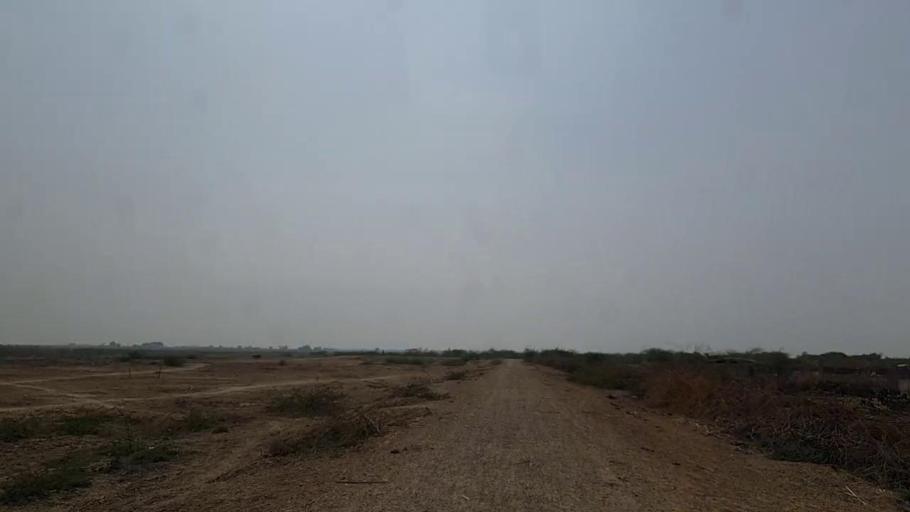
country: PK
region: Sindh
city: Naukot
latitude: 24.7948
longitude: 69.3308
